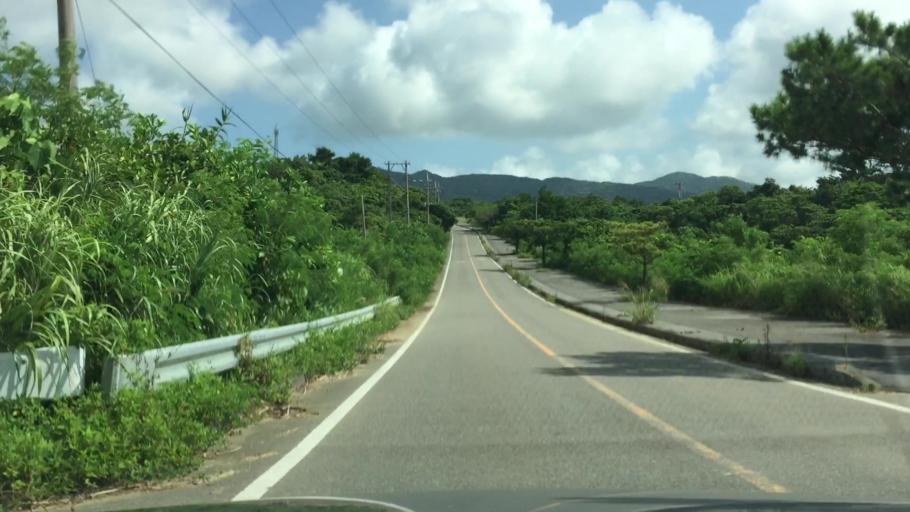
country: JP
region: Okinawa
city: Ishigaki
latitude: 24.4159
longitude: 124.2149
